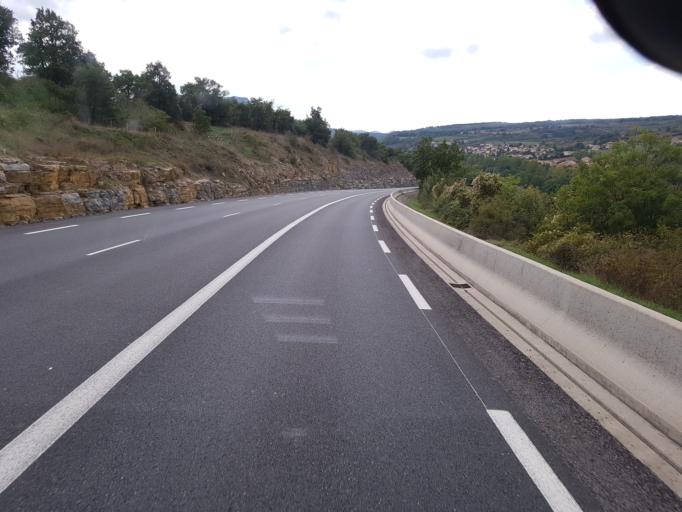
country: FR
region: Midi-Pyrenees
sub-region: Departement de l'Aveyron
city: Saint-Georges-de-Luzencon
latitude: 44.0738
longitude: 2.9892
